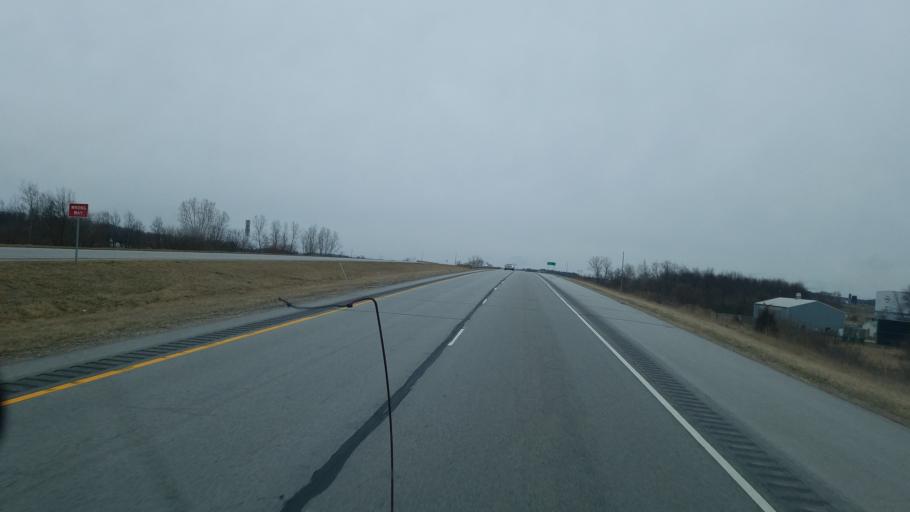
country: US
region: Indiana
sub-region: Marshall County
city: Argos
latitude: 41.2368
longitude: -86.2615
